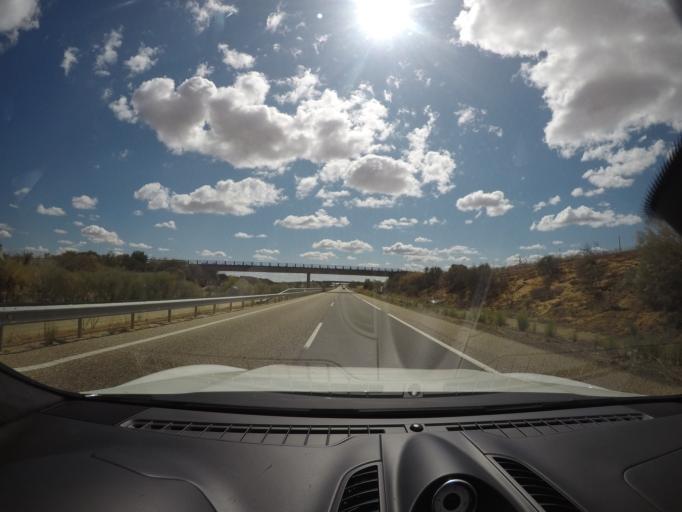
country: ES
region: Castille and Leon
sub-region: Provincia de Zamora
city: Matilla de Arzon
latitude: 42.0942
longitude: -5.6574
